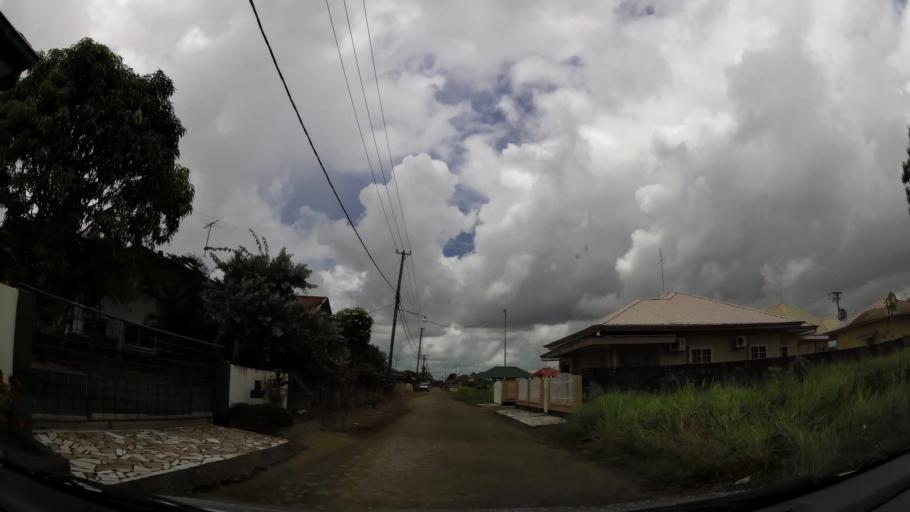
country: SR
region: Paramaribo
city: Paramaribo
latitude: 5.8258
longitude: -55.2224
